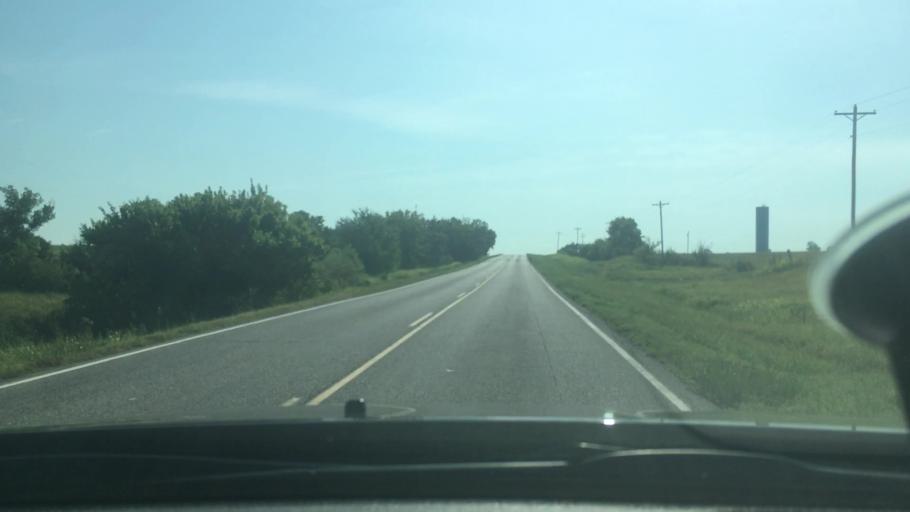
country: US
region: Oklahoma
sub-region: Garvin County
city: Pauls Valley
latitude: 34.6518
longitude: -97.2870
